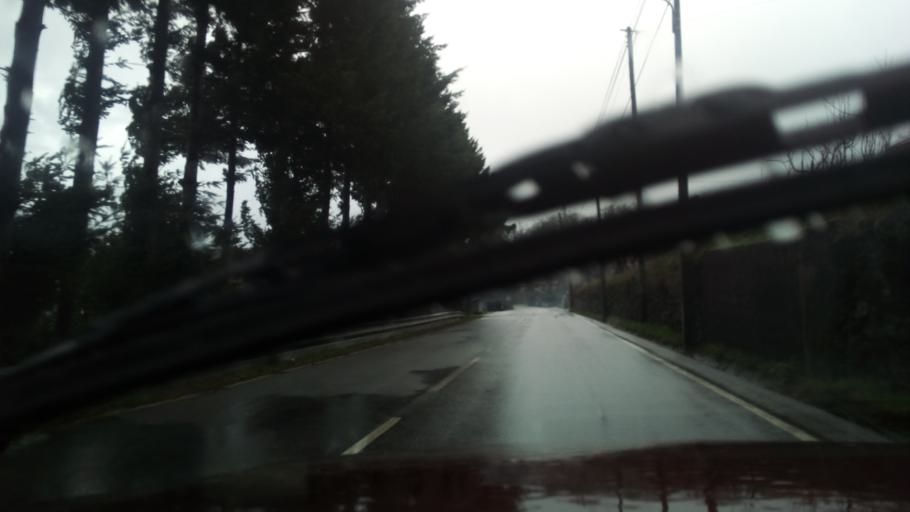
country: PT
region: Guarda
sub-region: Guarda
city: Guarda
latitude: 40.5431
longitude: -7.3174
